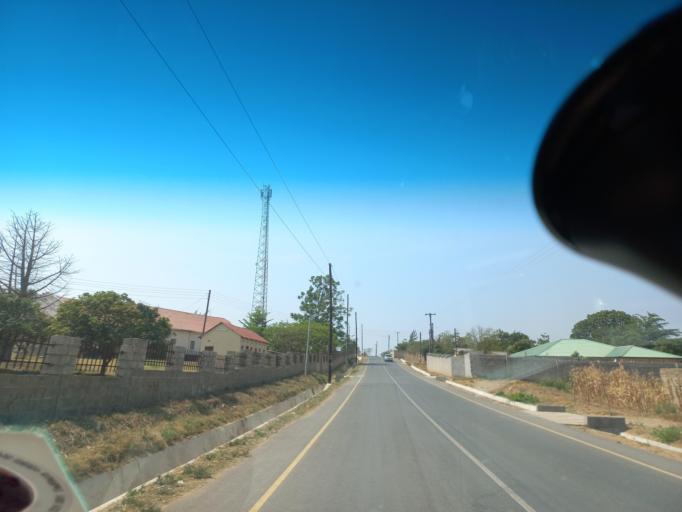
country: ZM
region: Lusaka
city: Lusaka
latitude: -15.5687
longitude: 28.2705
